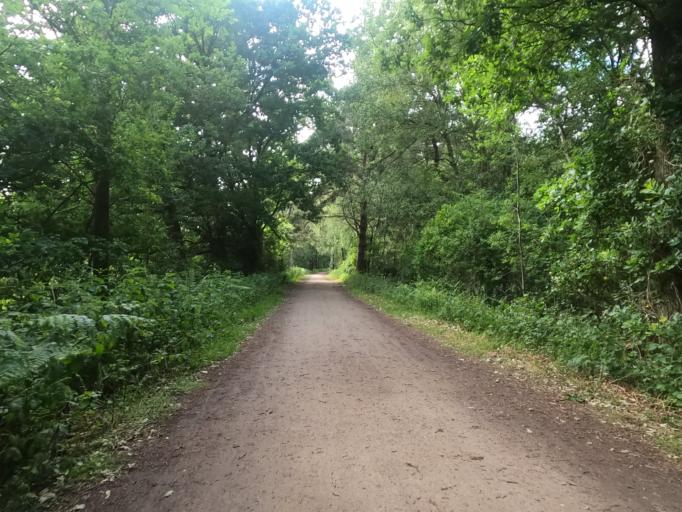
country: GB
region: England
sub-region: Cheshire West and Chester
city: Cuddington
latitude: 53.2152
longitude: -2.6017
